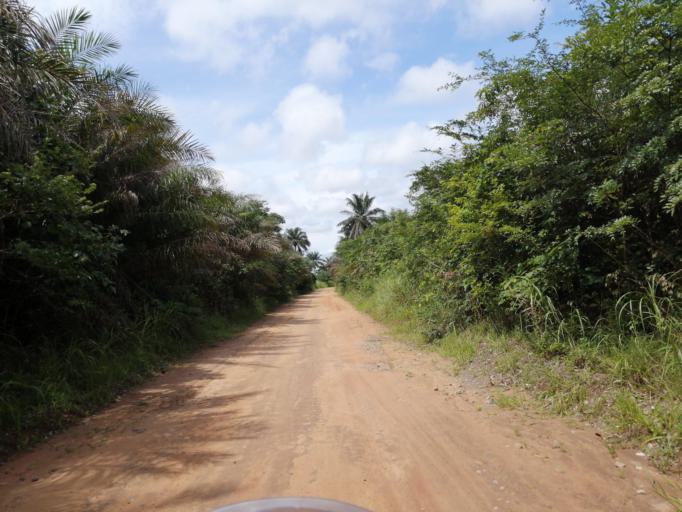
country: SL
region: Northern Province
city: Pepel
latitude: 8.6725
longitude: -13.0004
